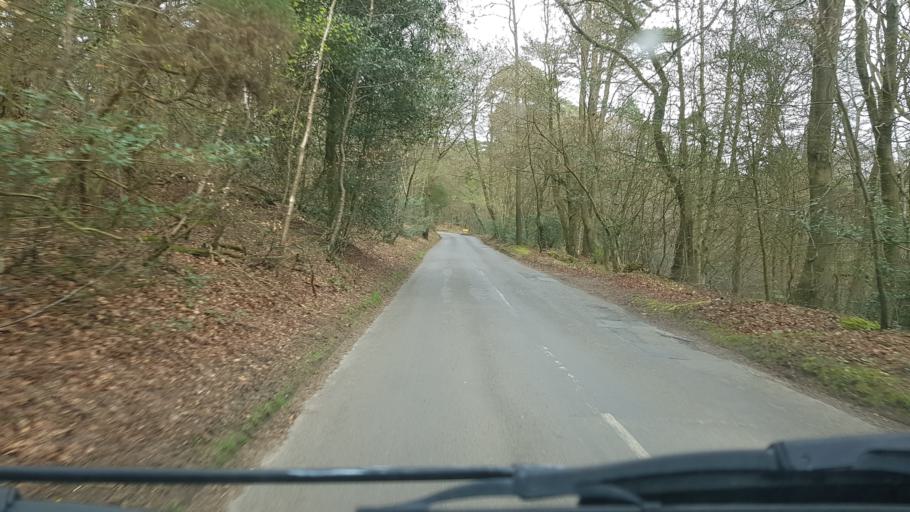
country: GB
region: England
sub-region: Surrey
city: Cranleigh
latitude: 51.1735
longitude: -0.4575
